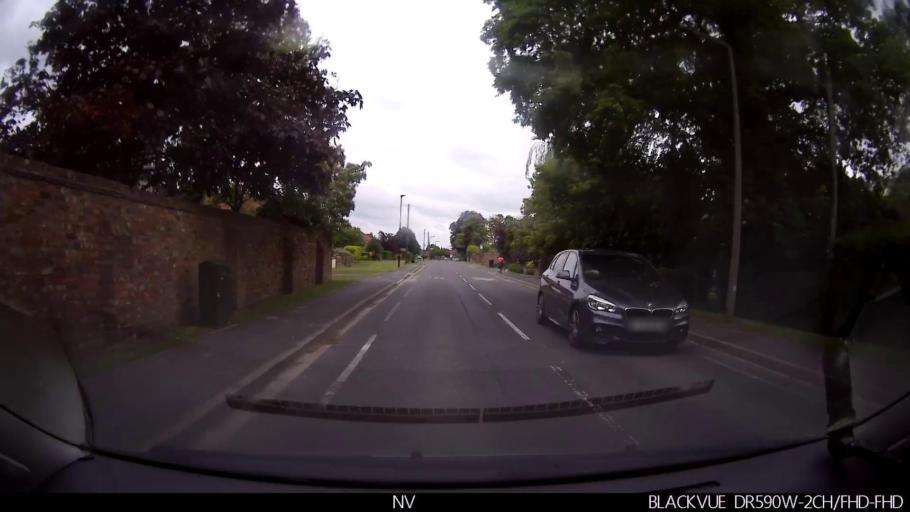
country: GB
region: England
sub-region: City of York
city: Haxby
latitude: 54.0088
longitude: -1.0737
